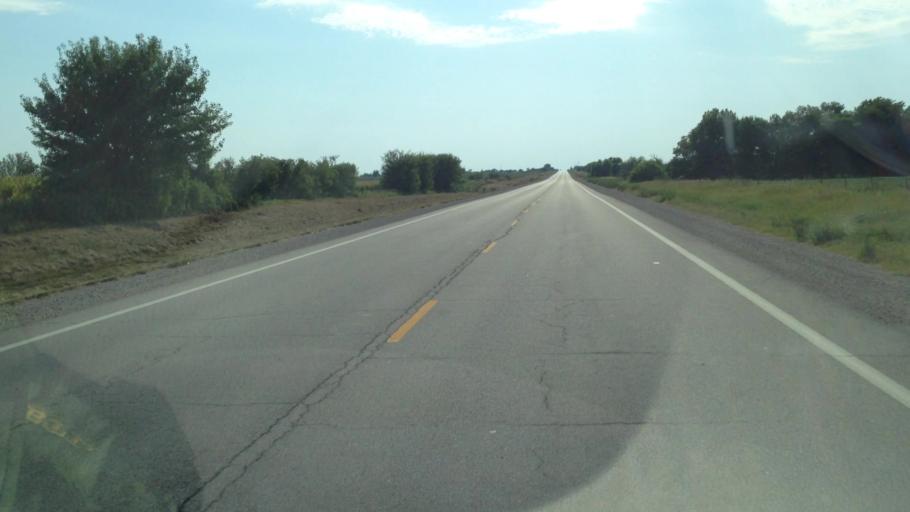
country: US
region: Kansas
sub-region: Anderson County
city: Garnett
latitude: 38.0816
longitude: -95.1942
